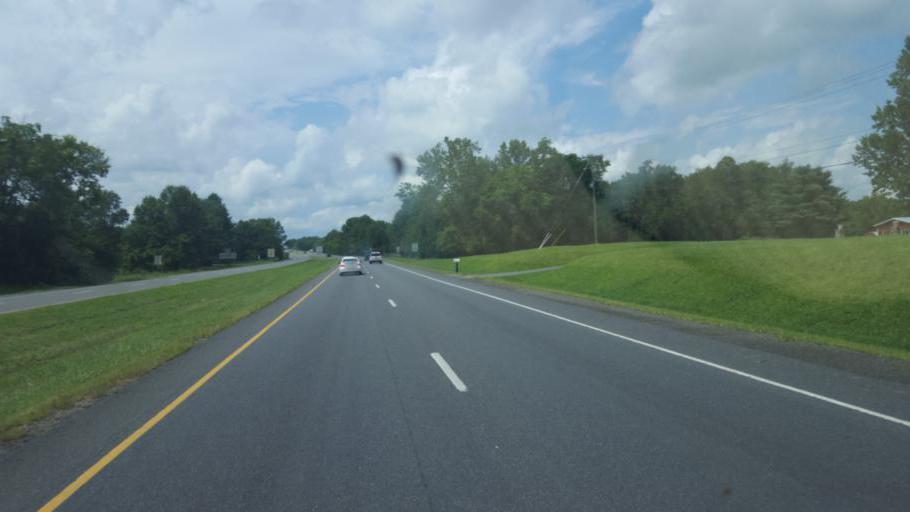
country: US
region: Virginia
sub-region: Fauquier County
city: Marshall
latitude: 38.8534
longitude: -77.8370
